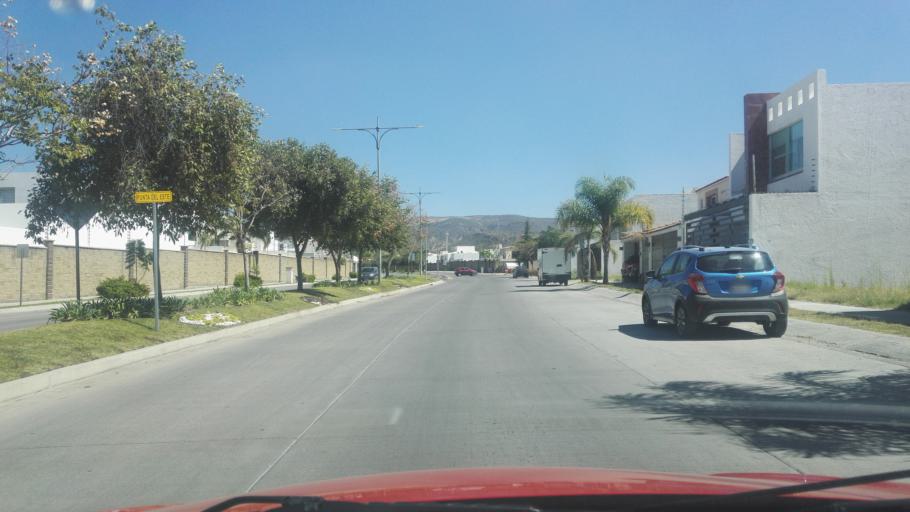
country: MX
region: Guanajuato
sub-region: Leon
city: Medina
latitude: 21.1275
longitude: -101.6090
